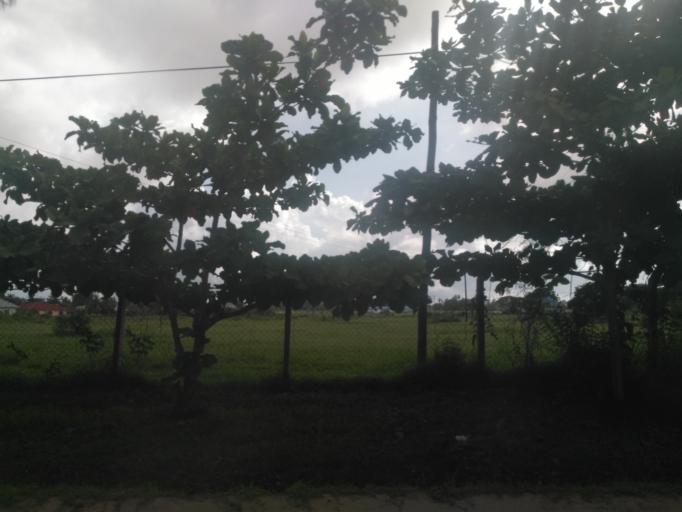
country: TZ
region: Zanzibar Urban/West
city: Zanzibar
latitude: -6.2157
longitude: 39.2199
